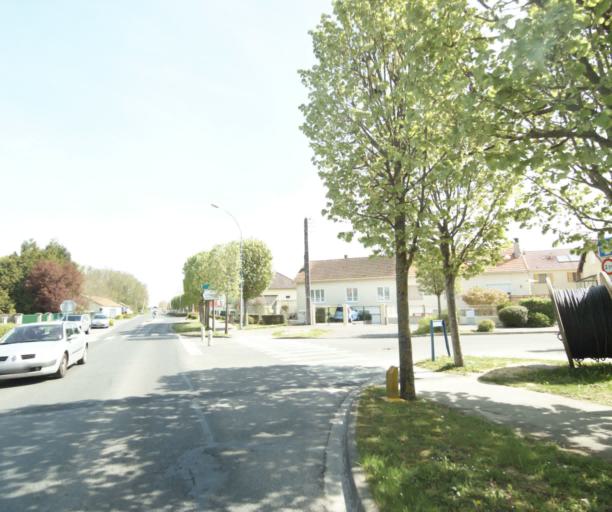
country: FR
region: Ile-de-France
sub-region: Departement de Seine-et-Marne
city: Nangis
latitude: 48.5573
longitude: 3.0232
